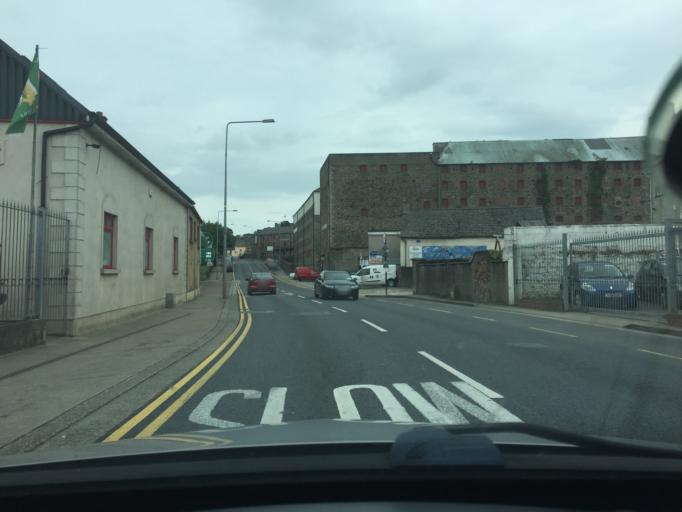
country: IE
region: Leinster
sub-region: Loch Garman
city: Enniscorthy
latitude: 52.5041
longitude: -6.5694
